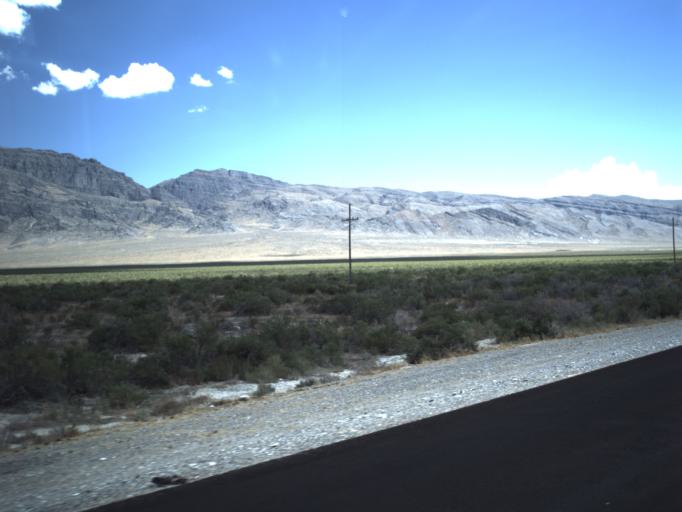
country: US
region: Utah
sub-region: Beaver County
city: Milford
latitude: 39.0801
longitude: -113.4871
